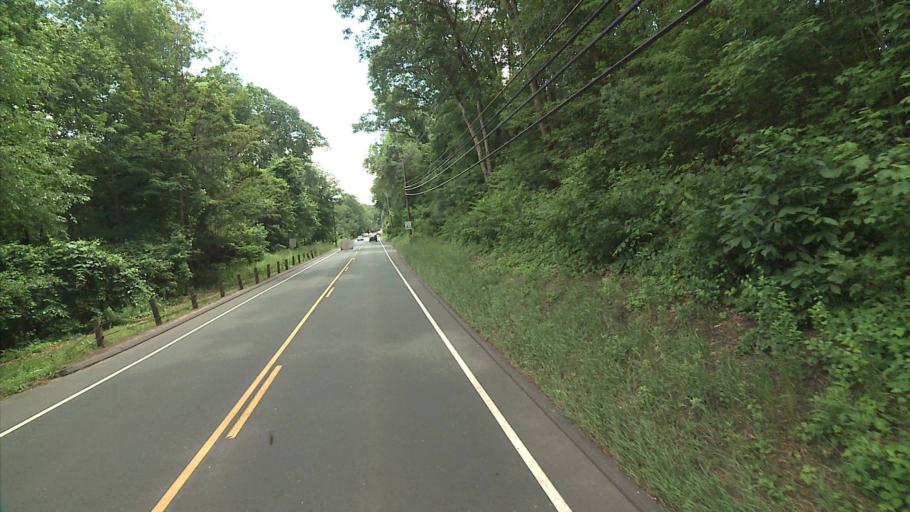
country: US
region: Connecticut
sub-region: Litchfield County
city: Oakville
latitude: 41.5834
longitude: -73.1020
